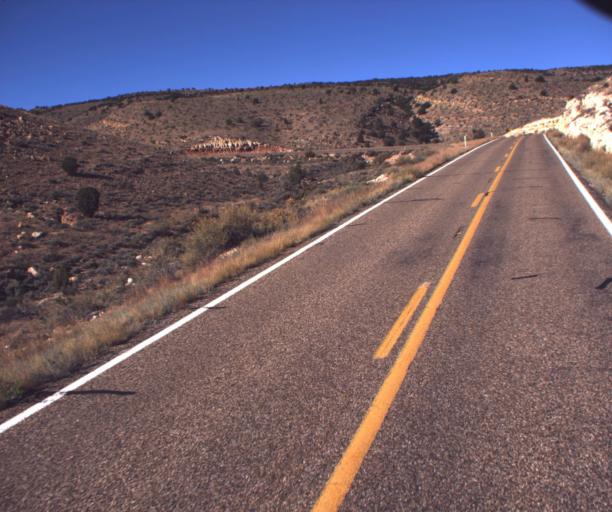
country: US
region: Arizona
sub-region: Coconino County
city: Fredonia
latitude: 36.7337
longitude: -112.0596
